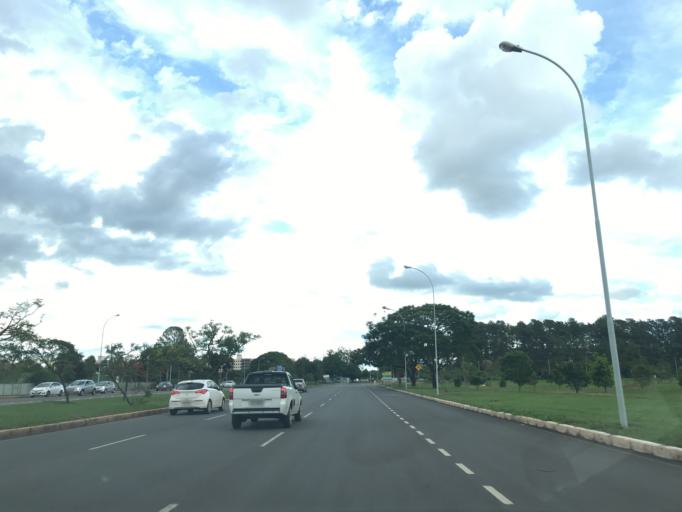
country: BR
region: Federal District
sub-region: Brasilia
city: Brasilia
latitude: -15.8100
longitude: -47.9265
